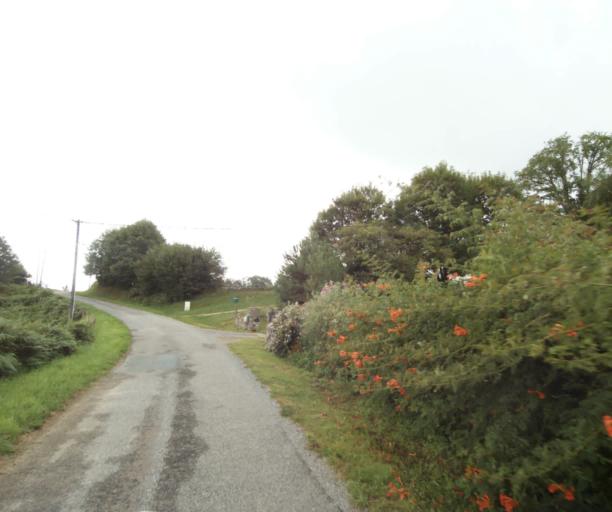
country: FR
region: Limousin
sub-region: Departement de la Correze
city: Sainte-Fortunade
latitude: 45.1969
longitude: 1.8008
